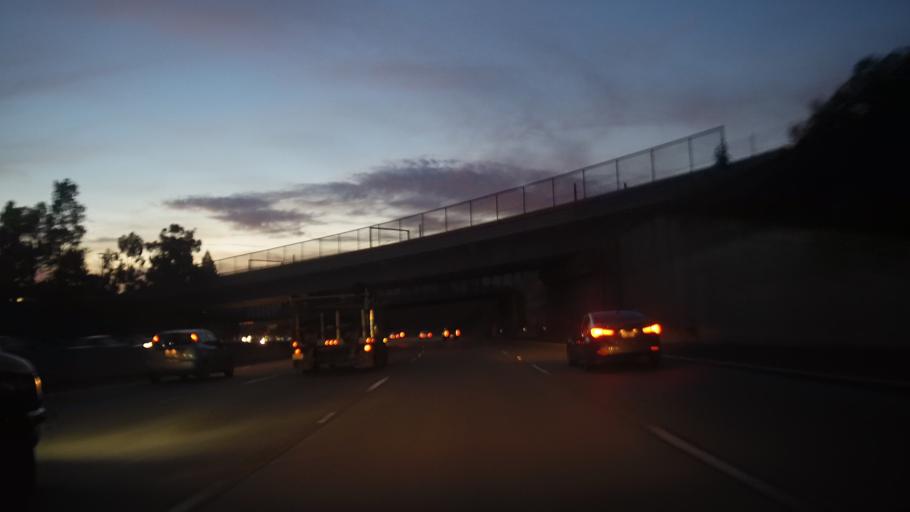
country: US
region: California
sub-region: San Diego County
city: Lemon Grove
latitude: 32.7485
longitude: -117.0259
